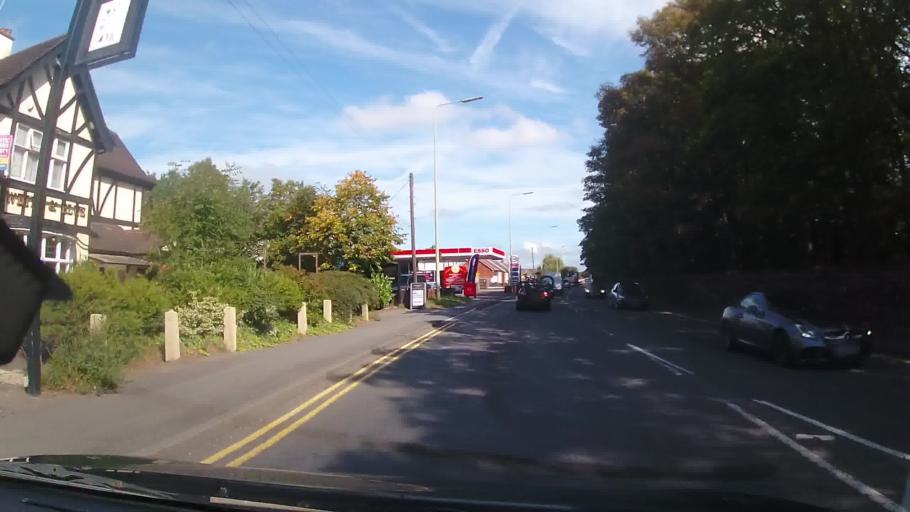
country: GB
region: England
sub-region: Staffordshire
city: Featherstone
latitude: 52.6442
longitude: -2.0865
